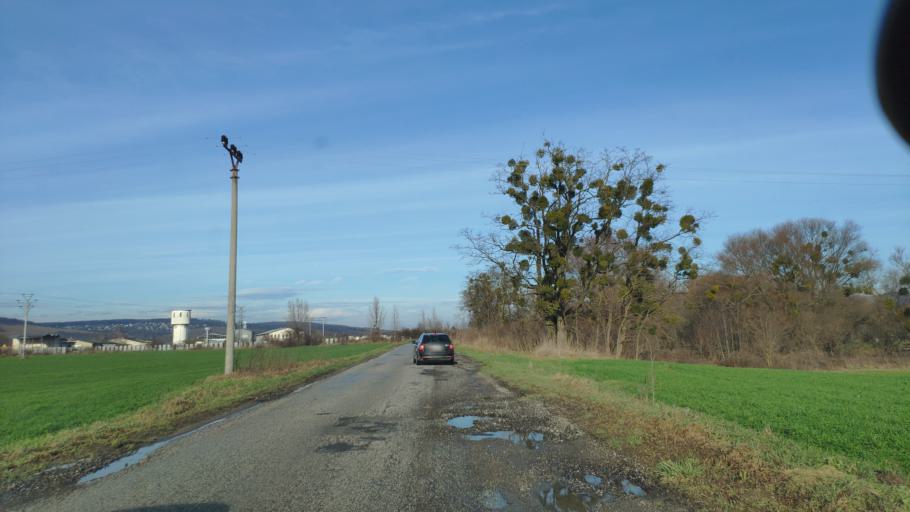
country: SK
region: Kosicky
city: Kosice
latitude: 48.6918
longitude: 21.3399
